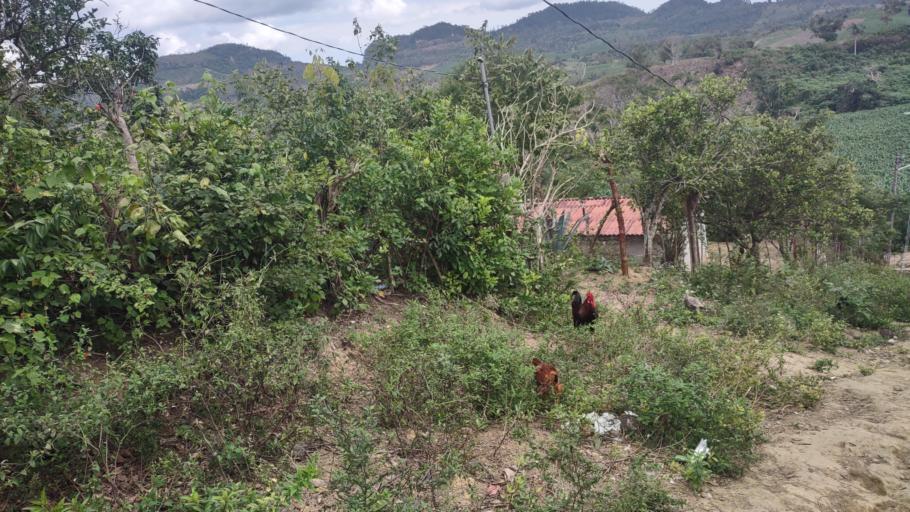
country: MX
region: Veracruz
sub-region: Papantla
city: Polutla
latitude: 20.4654
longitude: -97.2561
